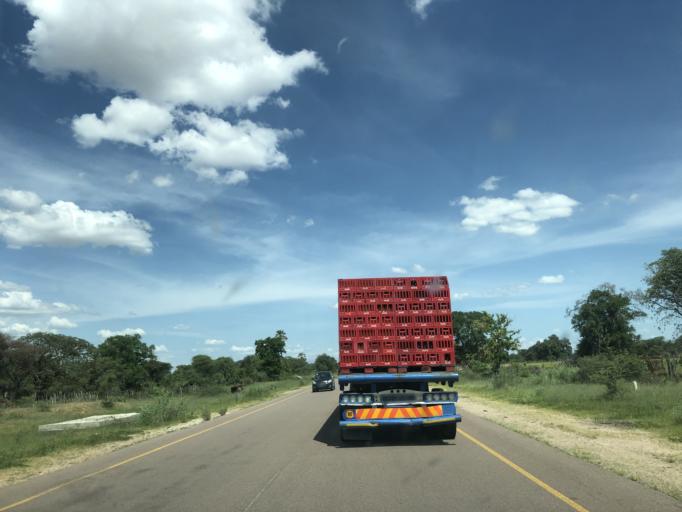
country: AO
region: Cunene
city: Ondjiva
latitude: -16.8948
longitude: 15.5017
